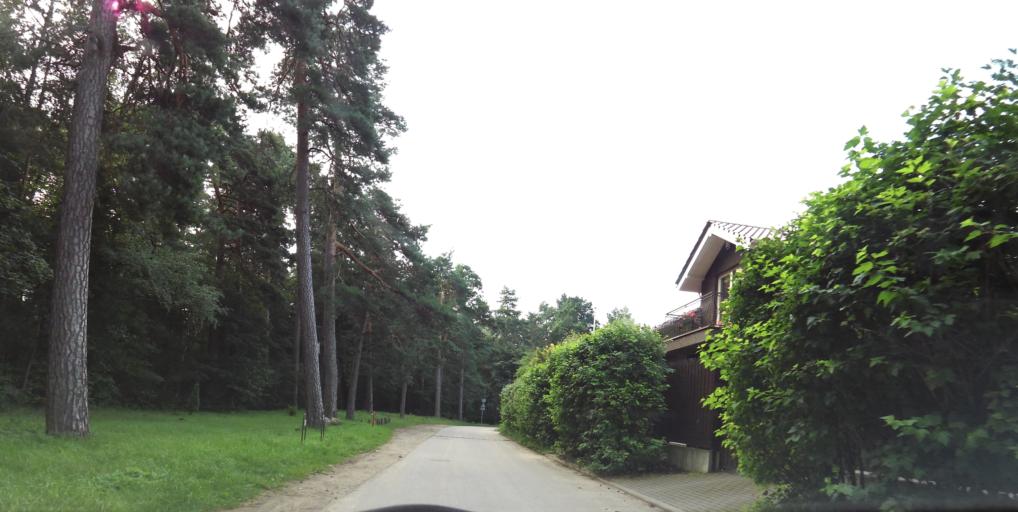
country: LT
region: Vilnius County
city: Seskine
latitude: 54.7338
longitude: 25.2843
